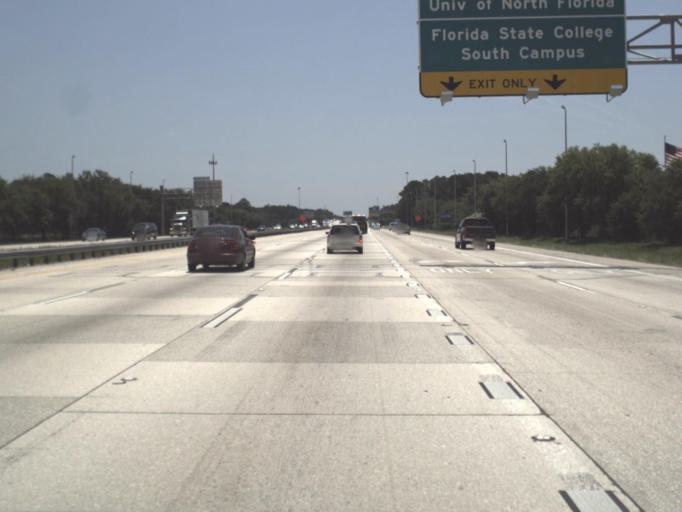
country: US
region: Florida
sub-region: Duval County
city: Jacksonville
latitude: 30.2553
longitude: -81.6007
